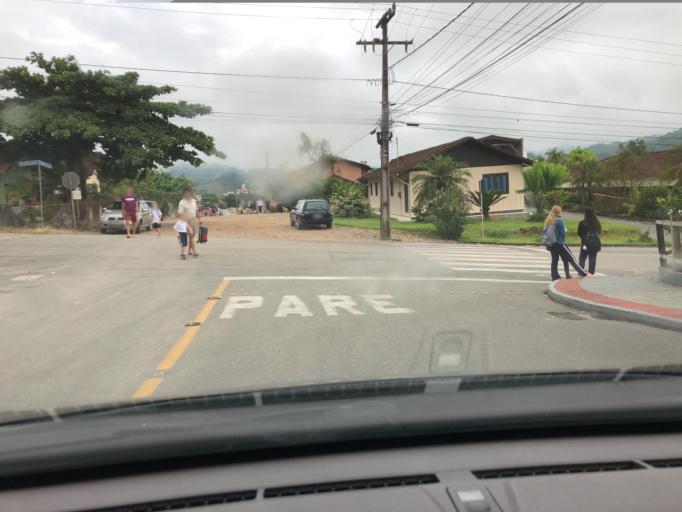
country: BR
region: Santa Catarina
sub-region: Jaragua Do Sul
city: Jaragua do Sul
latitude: -26.5098
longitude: -49.1387
